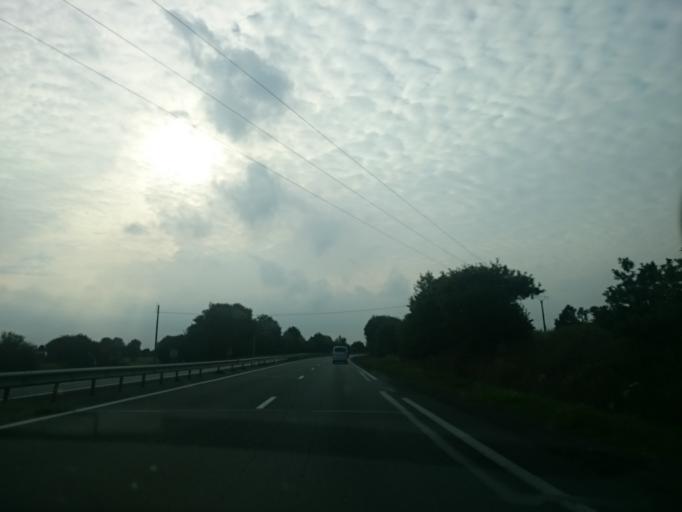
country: FR
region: Brittany
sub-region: Departement des Cotes-d'Armor
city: Pedernec
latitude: 48.5683
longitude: -3.2943
